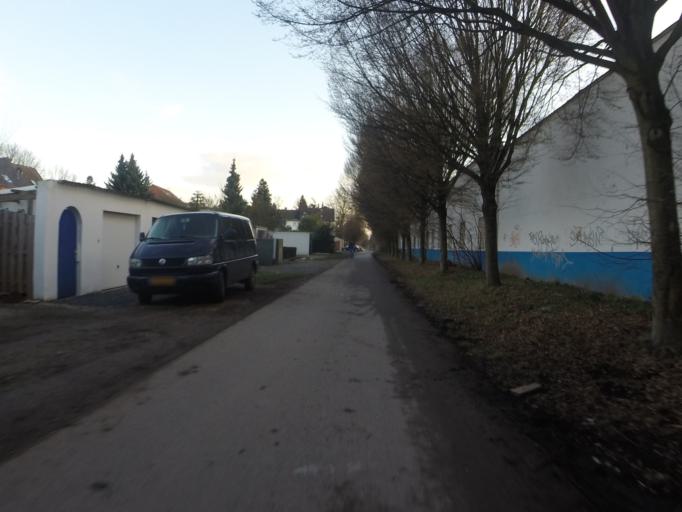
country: NL
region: Limburg
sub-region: Gemeente Kerkrade
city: Kerkrade
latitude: 50.8309
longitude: 6.0854
